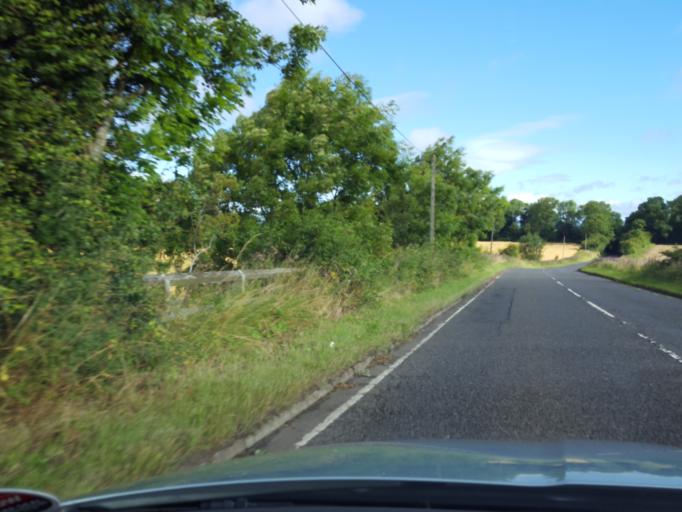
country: GB
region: Scotland
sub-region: West Lothian
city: Broxburn
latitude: 55.9571
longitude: -3.5094
